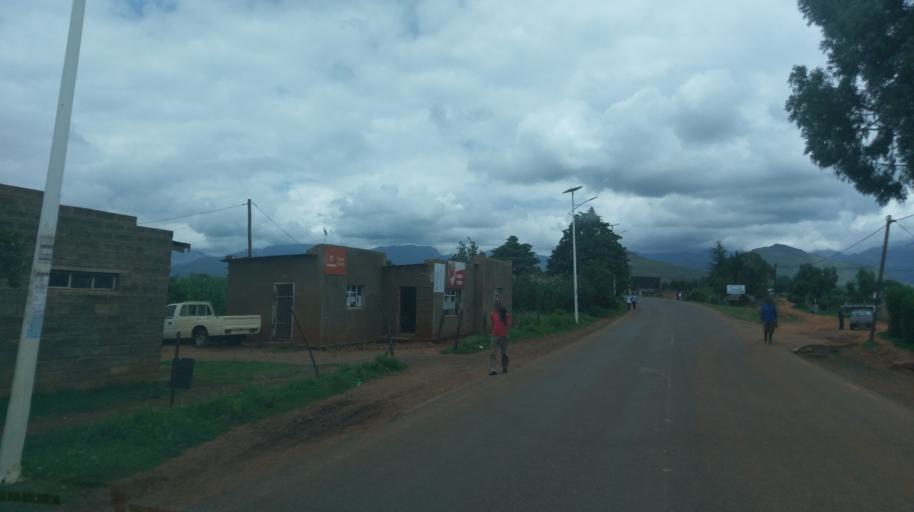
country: LS
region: Leribe
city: Leribe
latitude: -29.0067
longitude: 28.2130
